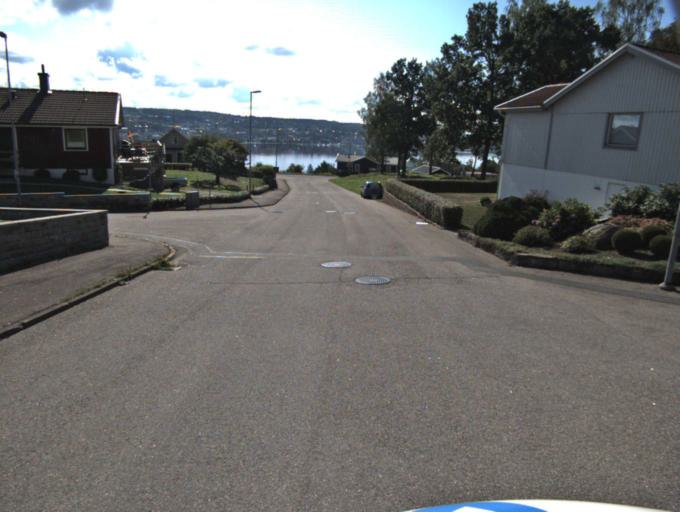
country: SE
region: Vaestra Goetaland
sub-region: Ulricehamns Kommun
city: Ulricehamn
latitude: 57.8041
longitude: 13.3964
